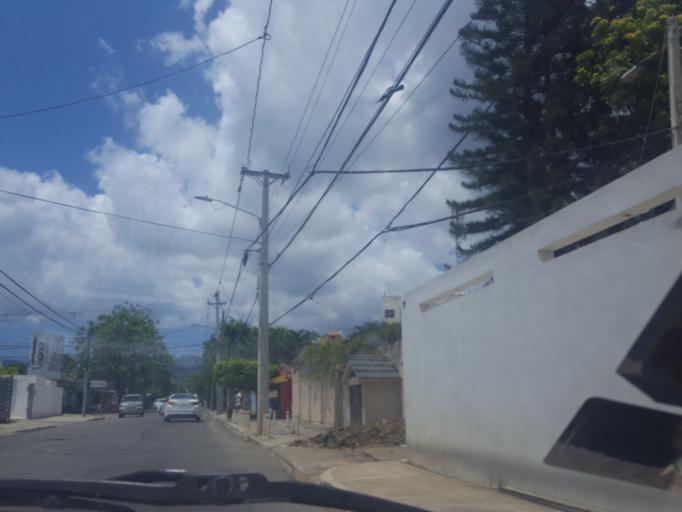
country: DO
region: Santiago
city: Santiago de los Caballeros
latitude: 19.4728
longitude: -70.6633
